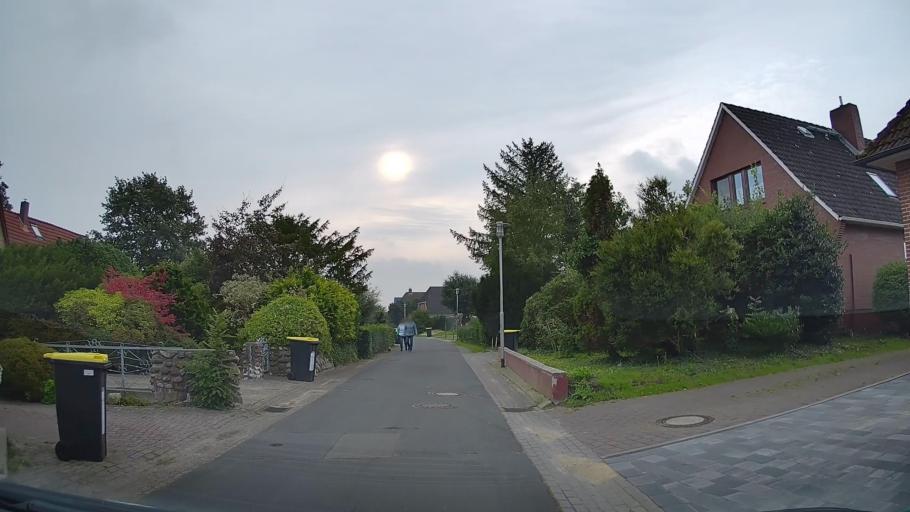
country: DE
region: Lower Saxony
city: Cuxhaven
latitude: 53.8299
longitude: 8.7615
